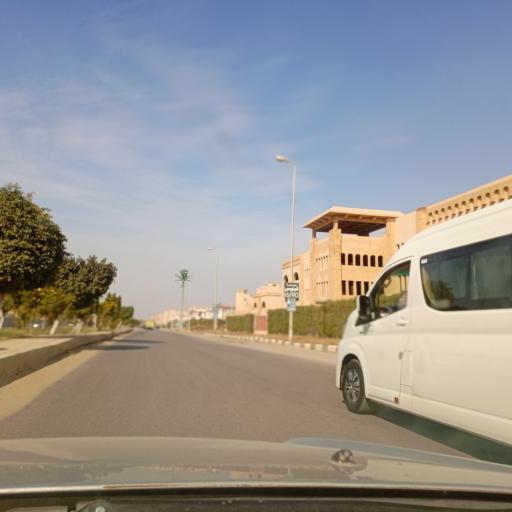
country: EG
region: Muhafazat al Qalyubiyah
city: Al Khankah
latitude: 30.0361
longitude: 31.4852
